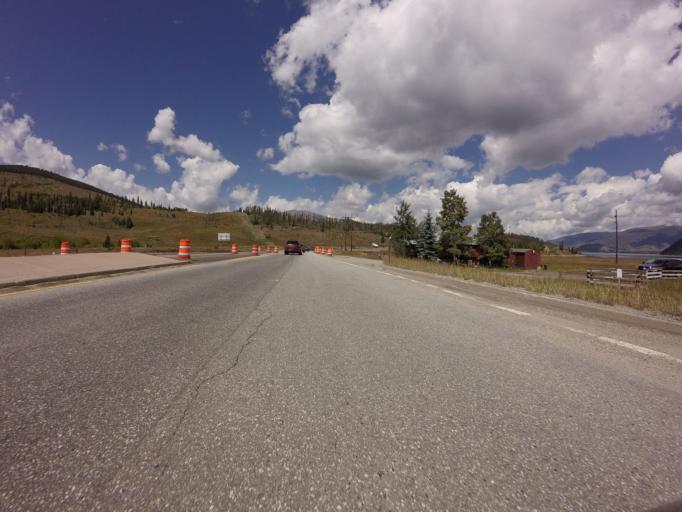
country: US
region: Colorado
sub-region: Summit County
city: Frisco
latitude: 39.5676
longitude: -106.0549
